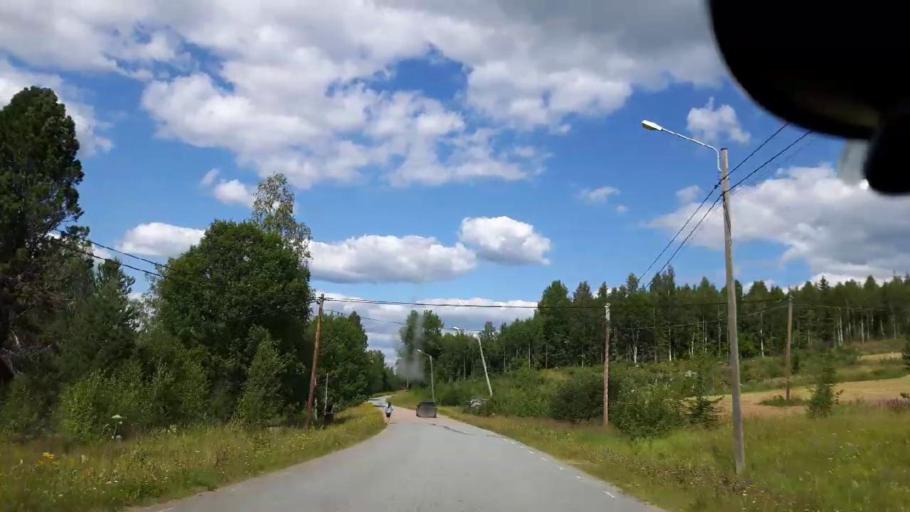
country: SE
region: Jaemtland
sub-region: Ragunda Kommun
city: Hammarstrand
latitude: 62.9428
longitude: 16.6918
